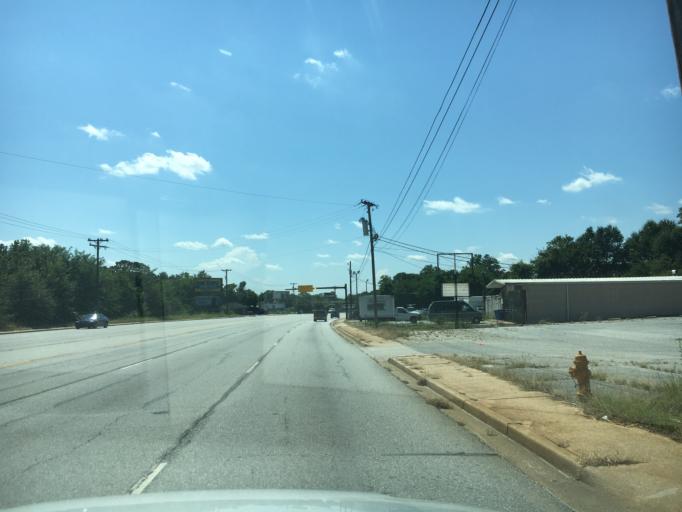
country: US
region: South Carolina
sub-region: Greenville County
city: Greenville
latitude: 34.8876
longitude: -82.3885
